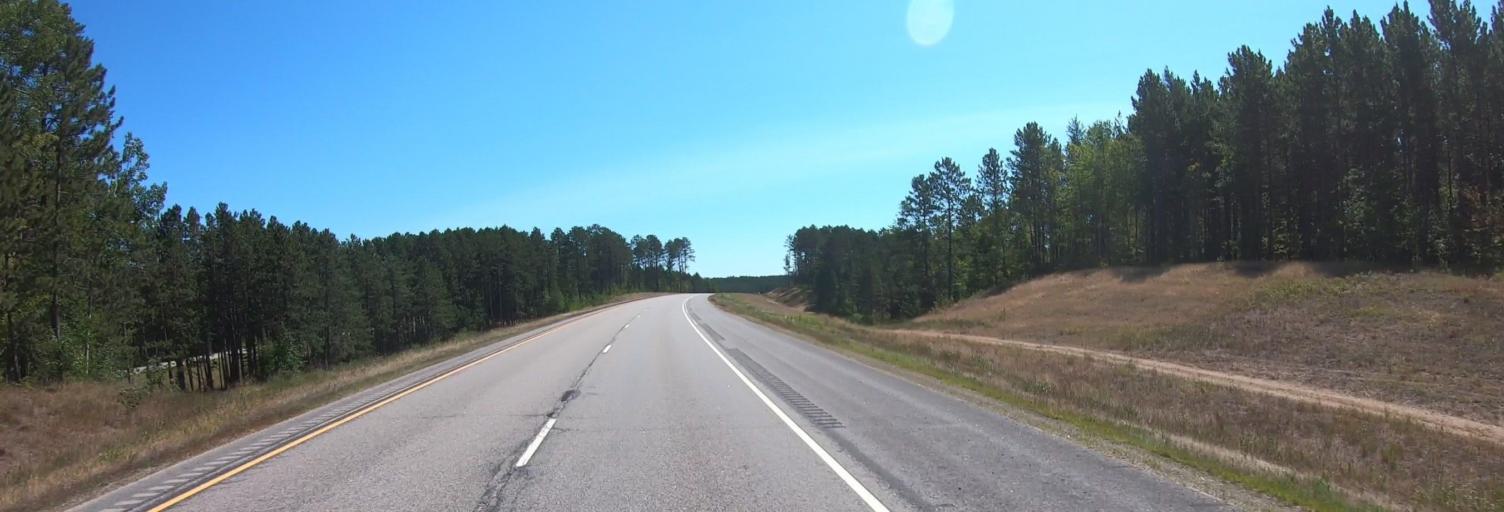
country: US
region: Minnesota
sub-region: Saint Louis County
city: Parkville
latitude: 47.6613
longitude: -92.5863
